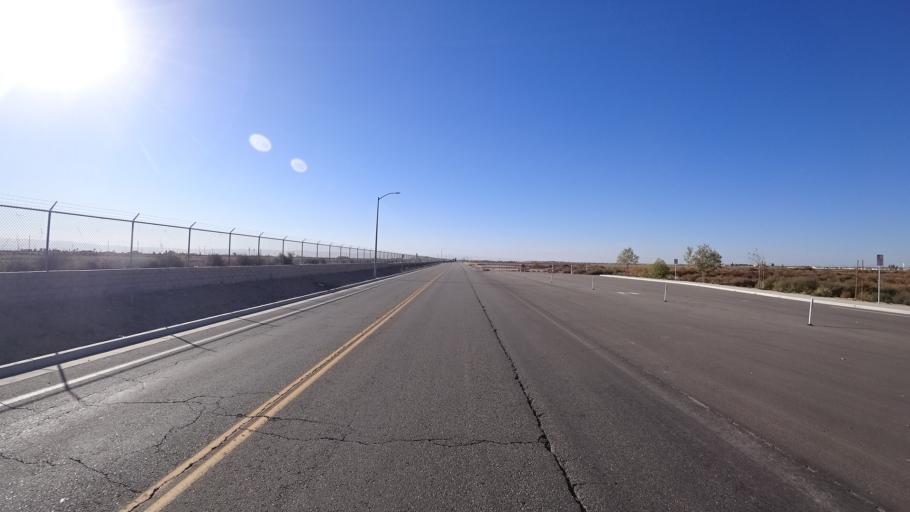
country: US
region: California
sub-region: Kern County
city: Greenfield
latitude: 35.2815
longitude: -119.0806
